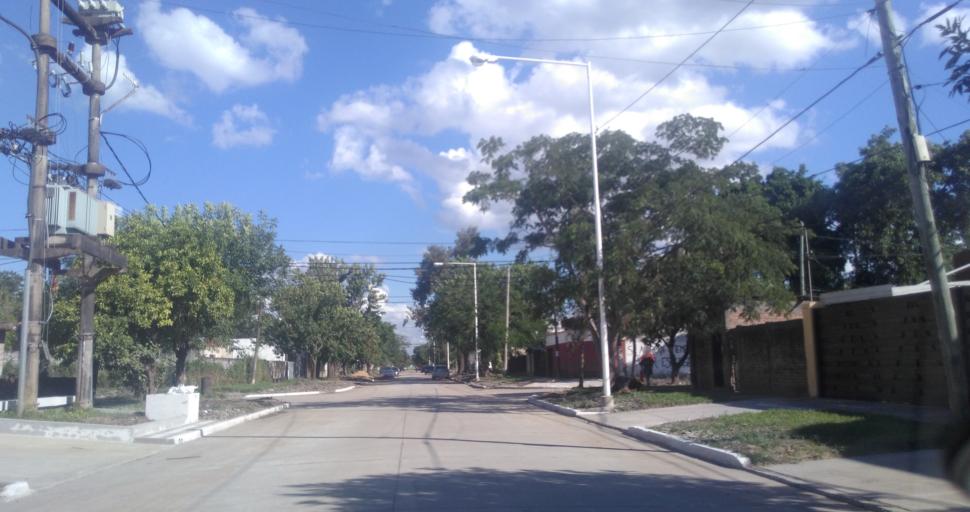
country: AR
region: Chaco
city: Resistencia
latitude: -27.4677
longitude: -58.9731
